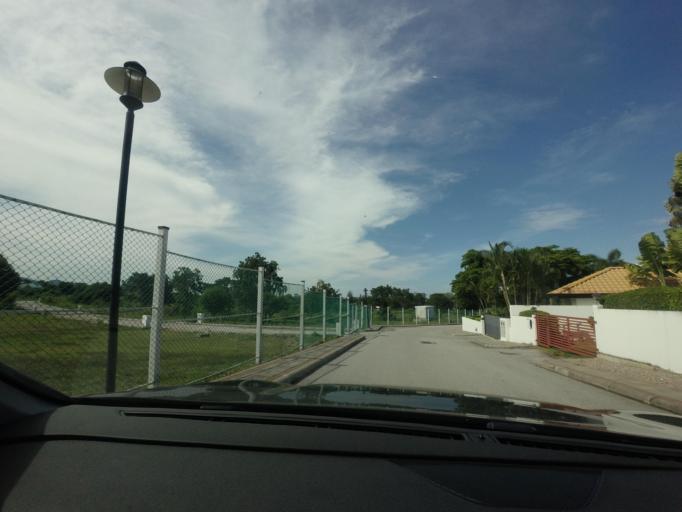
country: TH
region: Prachuap Khiri Khan
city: Hua Hin
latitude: 12.5162
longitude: 99.9591
